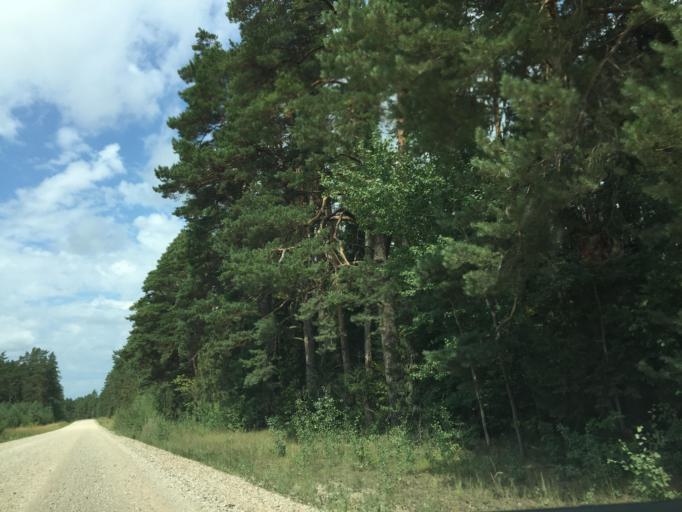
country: LV
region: Kandava
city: Kandava
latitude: 57.0311
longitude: 22.8116
